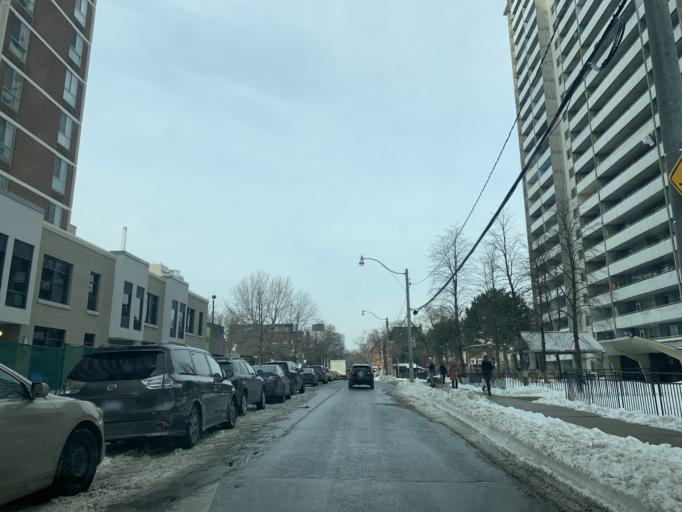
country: CA
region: Ontario
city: Toronto
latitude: 43.6700
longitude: -79.3748
